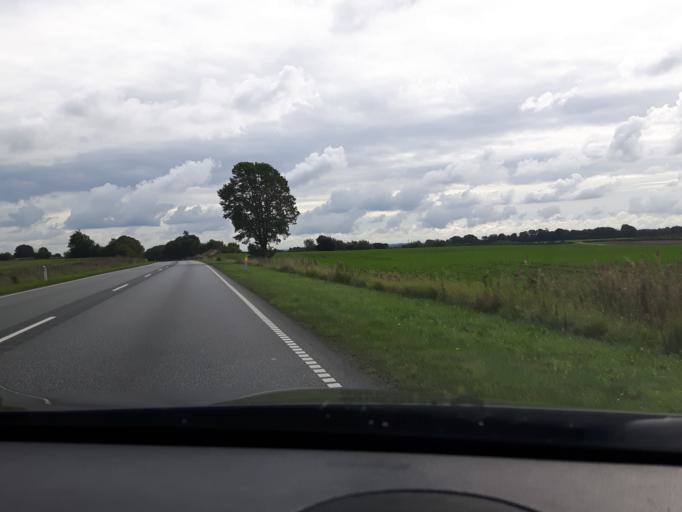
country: DK
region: South Denmark
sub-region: Vejle Kommune
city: Borkop
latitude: 55.6620
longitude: 9.6125
